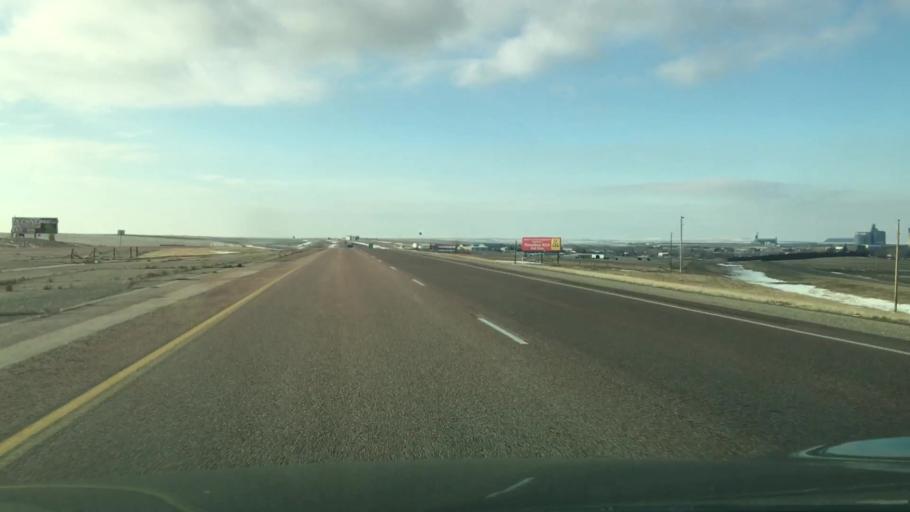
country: US
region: South Dakota
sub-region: Lyman County
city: Kennebec
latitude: 43.8913
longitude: -99.8501
